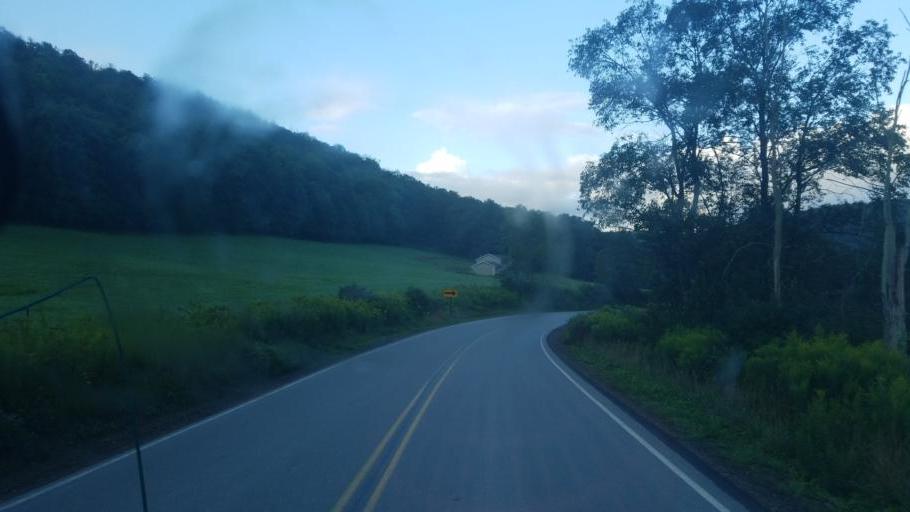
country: US
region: Pennsylvania
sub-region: Potter County
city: Galeton
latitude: 41.8409
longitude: -77.7869
